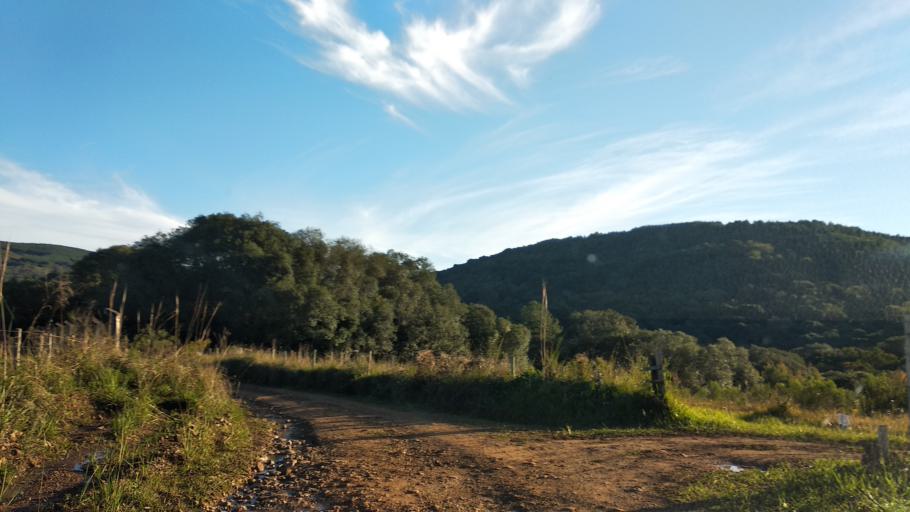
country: BR
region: Santa Catarina
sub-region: Celso Ramos
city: Celso Ramos
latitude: -27.5584
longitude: -51.2339
